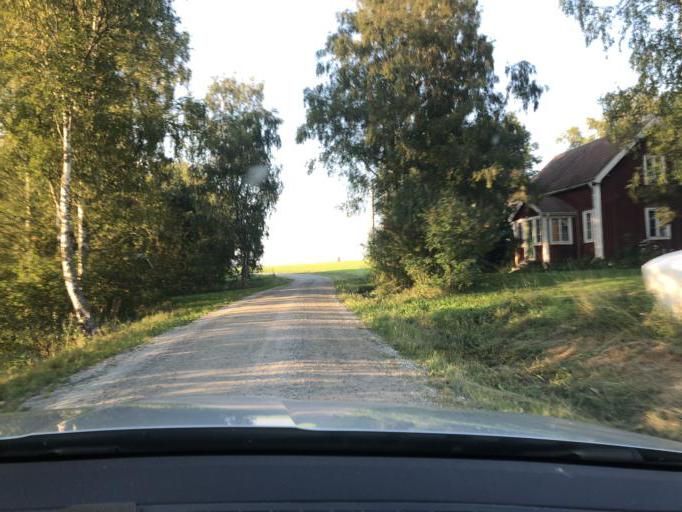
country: SE
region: Vaesternorrland
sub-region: Kramfors Kommun
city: Bollstabruk
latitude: 63.0733
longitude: 17.7361
